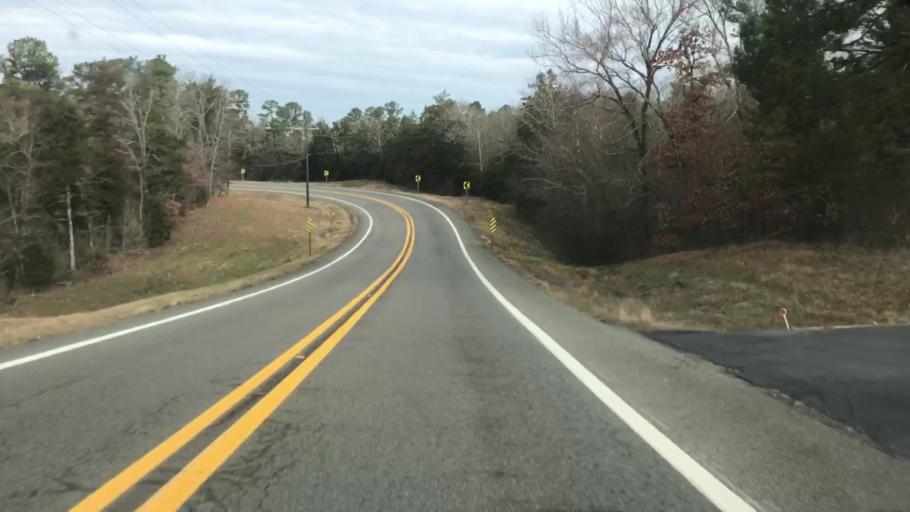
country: US
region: Arkansas
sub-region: Montgomery County
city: Mount Ida
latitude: 34.6180
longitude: -93.7038
